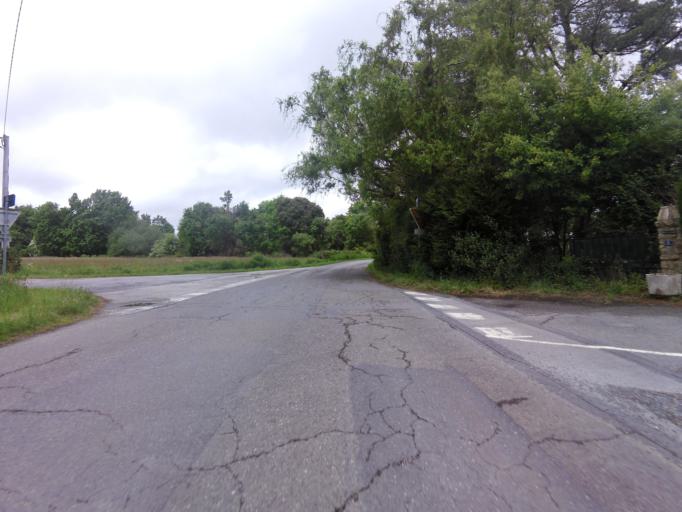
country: FR
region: Brittany
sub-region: Departement du Morbihan
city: Baden
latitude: 47.6024
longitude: -2.9381
